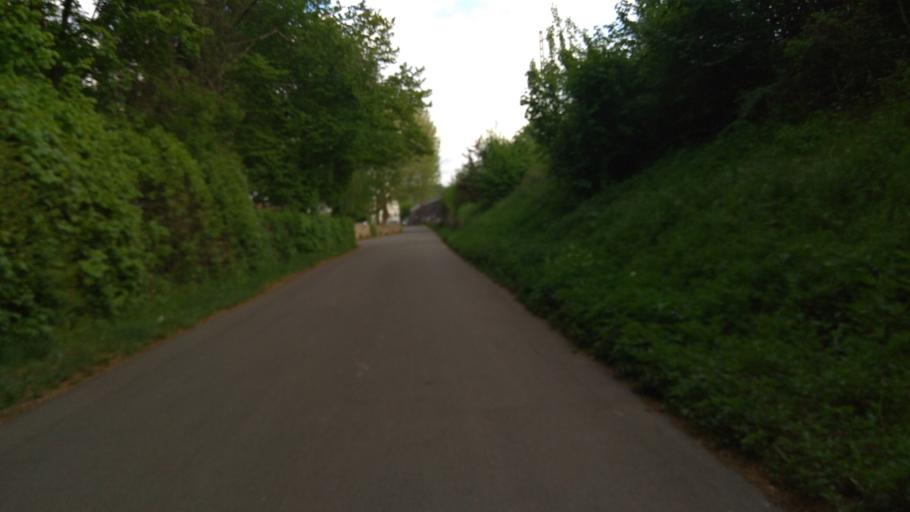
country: DE
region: Baden-Wuerttemberg
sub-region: Tuebingen Region
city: Wannweil
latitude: 48.4999
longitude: 9.1691
